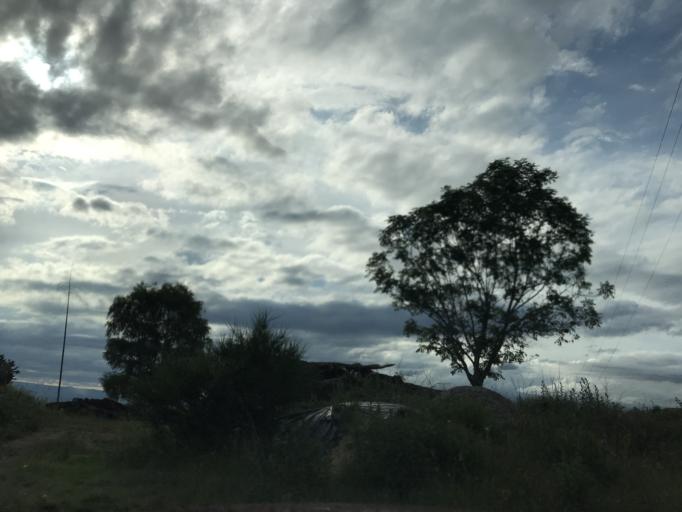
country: FR
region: Auvergne
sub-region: Departement du Puy-de-Dome
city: Thiers
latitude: 45.8539
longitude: 3.5612
